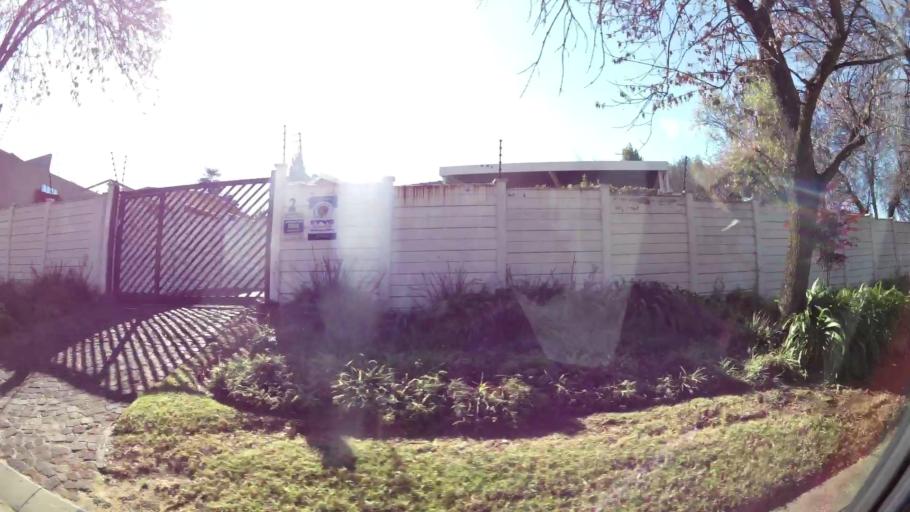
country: ZA
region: Gauteng
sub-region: City of Johannesburg Metropolitan Municipality
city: Roodepoort
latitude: -26.1004
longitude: 27.9591
